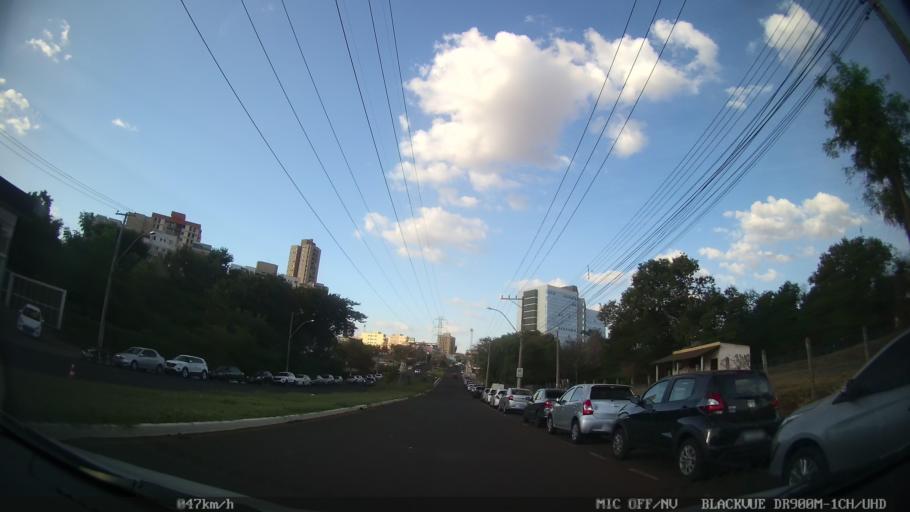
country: BR
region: Sao Paulo
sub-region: Ribeirao Preto
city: Ribeirao Preto
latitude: -21.1906
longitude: -47.7948
